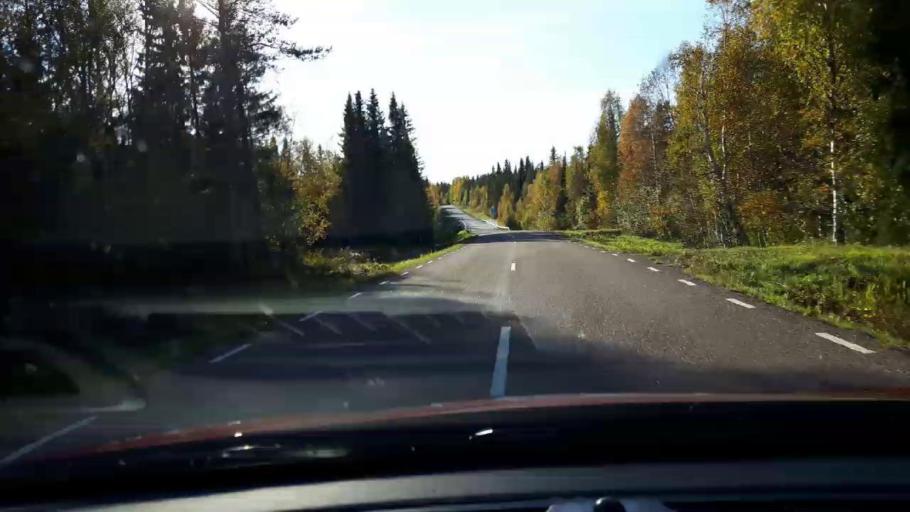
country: SE
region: Jaemtland
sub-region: Stroemsunds Kommun
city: Stroemsund
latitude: 63.8669
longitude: 15.1069
